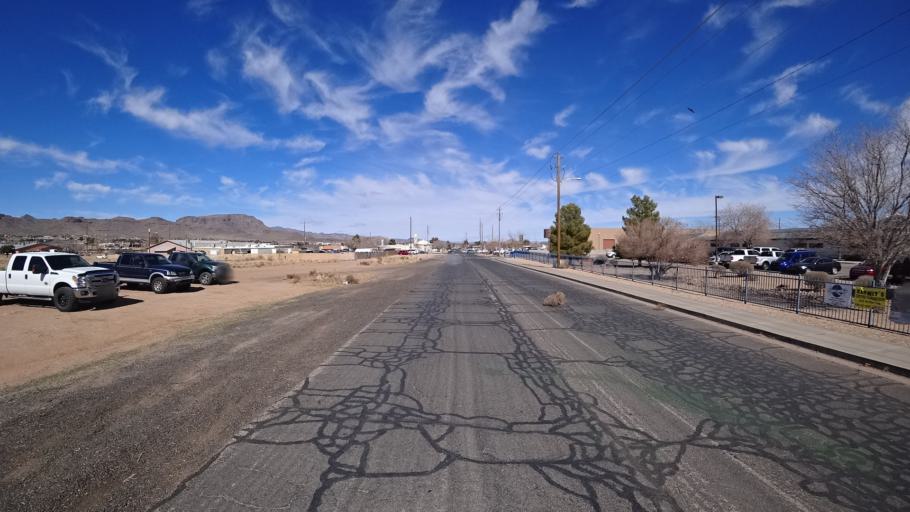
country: US
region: Arizona
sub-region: Mohave County
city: Kingman
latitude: 35.2233
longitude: -114.0292
